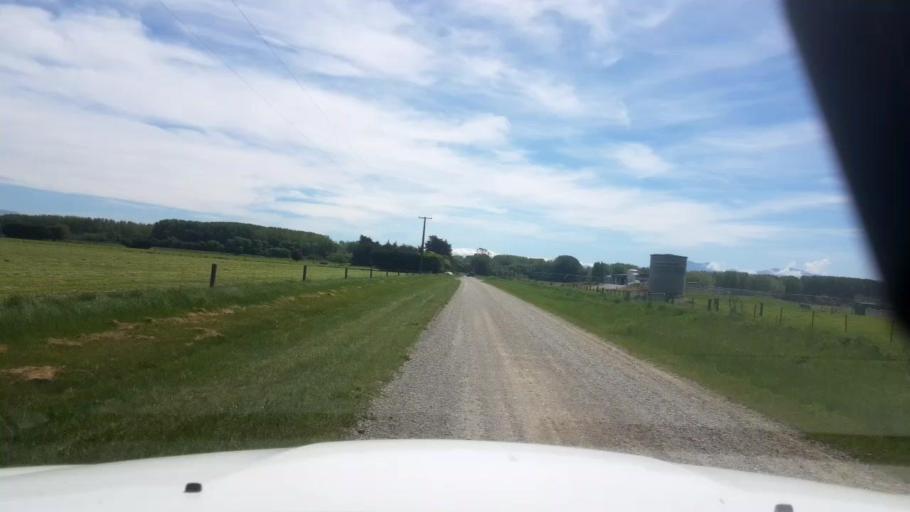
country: NZ
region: Canterbury
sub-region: Timaru District
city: Pleasant Point
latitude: -44.2644
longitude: 171.0962
